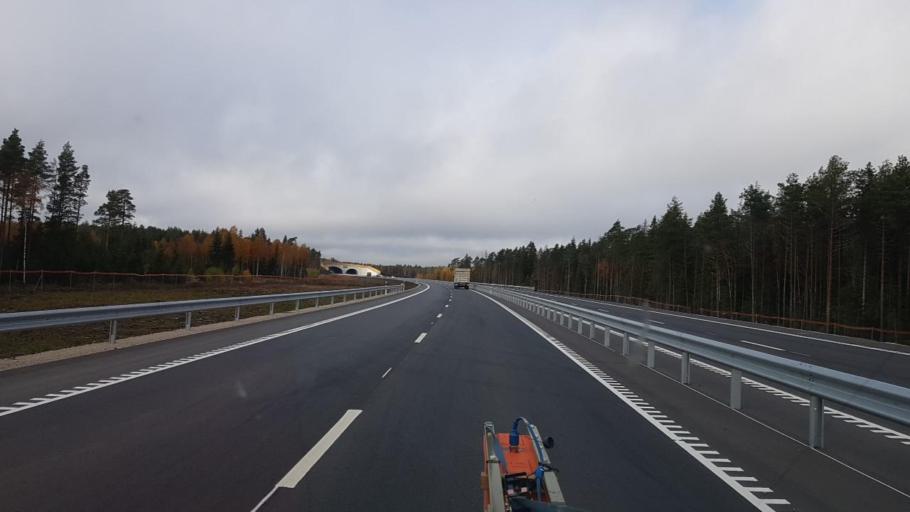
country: EE
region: Jaervamaa
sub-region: Paide linn
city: Paide
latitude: 59.0309
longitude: 25.5270
